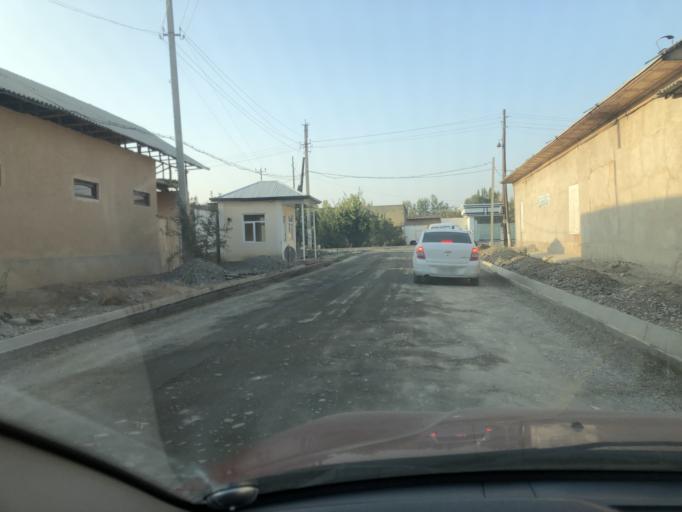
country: UZ
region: Namangan
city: Uychi
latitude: 41.0830
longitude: 71.9989
